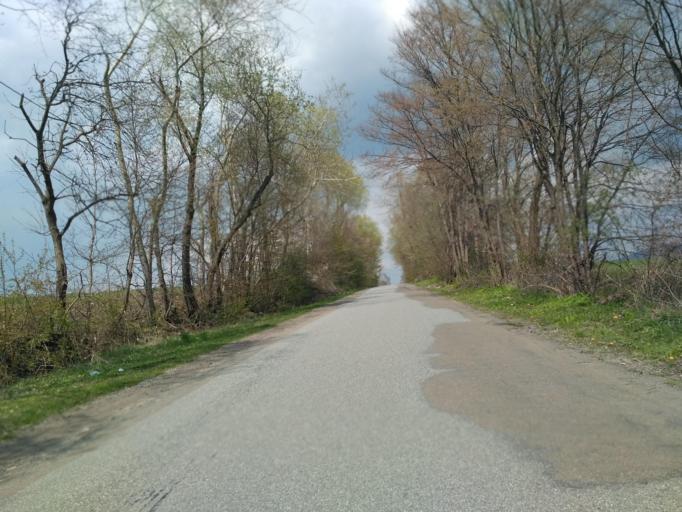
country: PL
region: Subcarpathian Voivodeship
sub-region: Powiat sanocki
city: Strachocina
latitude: 49.5727
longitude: 22.1215
